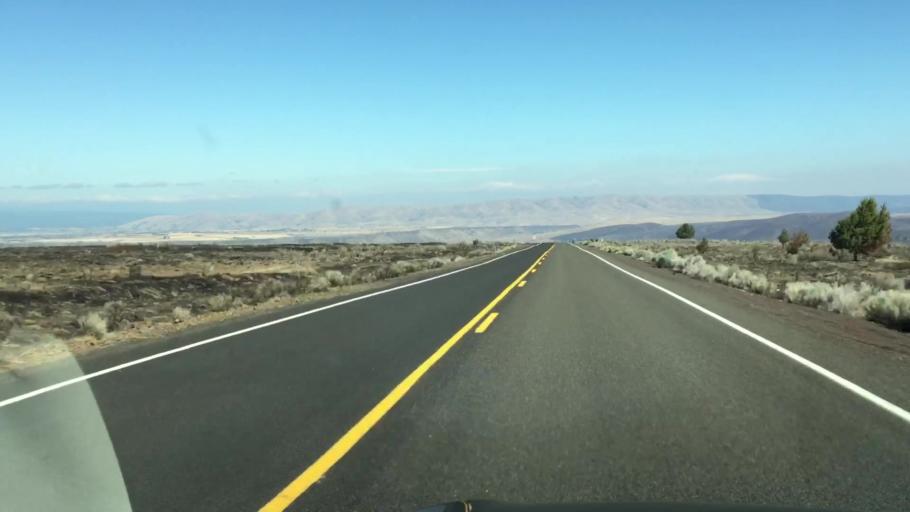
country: US
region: Oregon
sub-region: Jefferson County
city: Warm Springs
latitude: 45.0992
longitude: -121.0349
